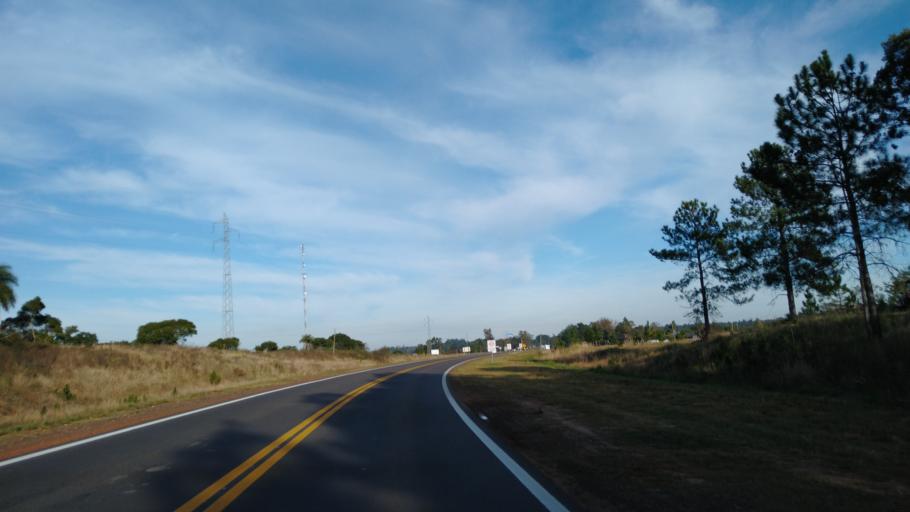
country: AR
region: Corrientes
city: Yapeyu
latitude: -29.4212
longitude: -56.8411
